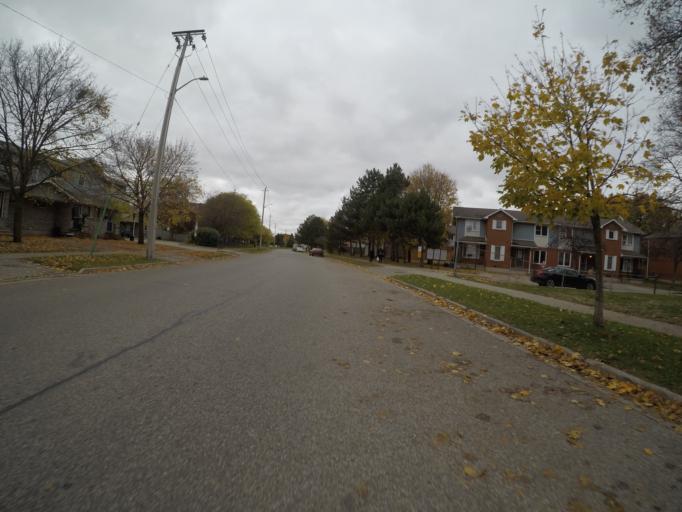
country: CA
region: Ontario
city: Kitchener
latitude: 43.4251
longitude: -80.4427
